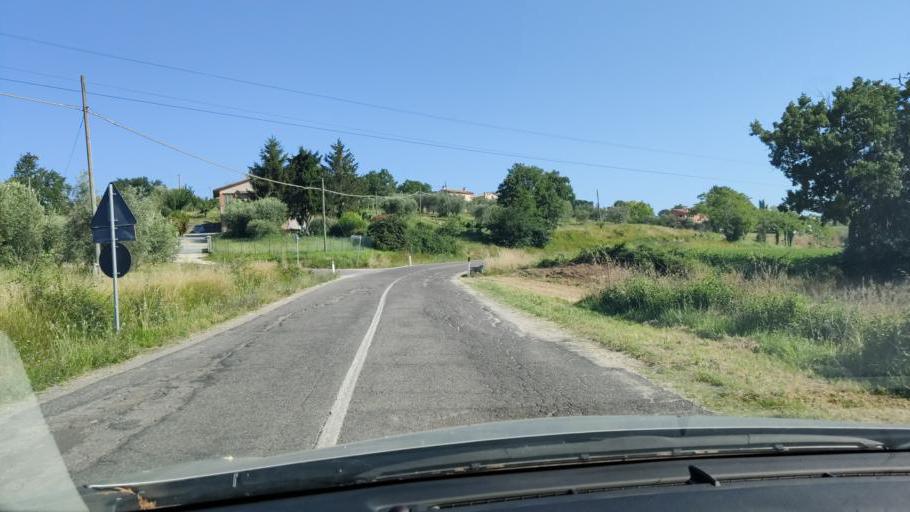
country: IT
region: Umbria
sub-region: Provincia di Terni
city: Avigliano Umbro
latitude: 42.6462
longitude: 12.4187
